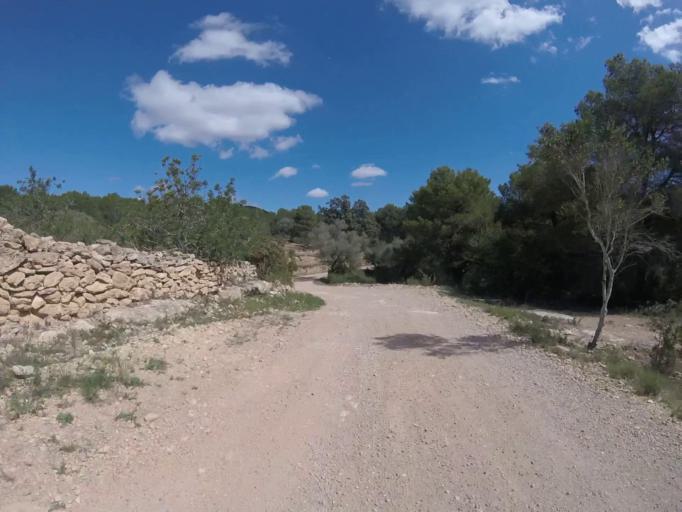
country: ES
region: Valencia
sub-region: Provincia de Castello
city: Santa Magdalena de Pulpis
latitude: 40.3154
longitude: 0.3304
